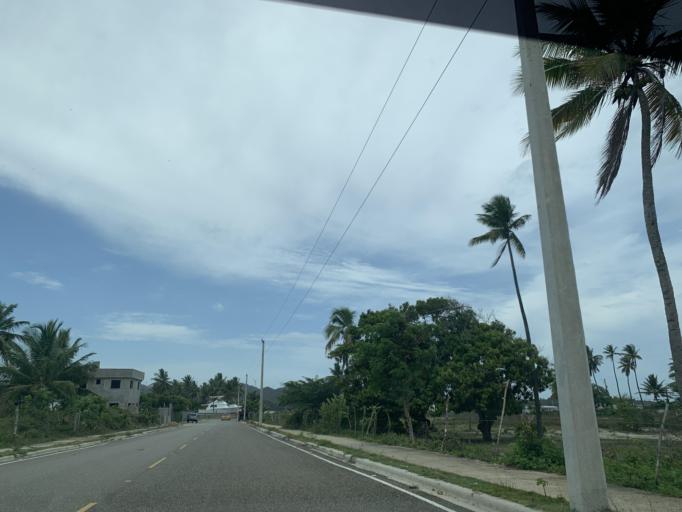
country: DO
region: Puerto Plata
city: Imbert
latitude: 19.8271
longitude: -70.7764
